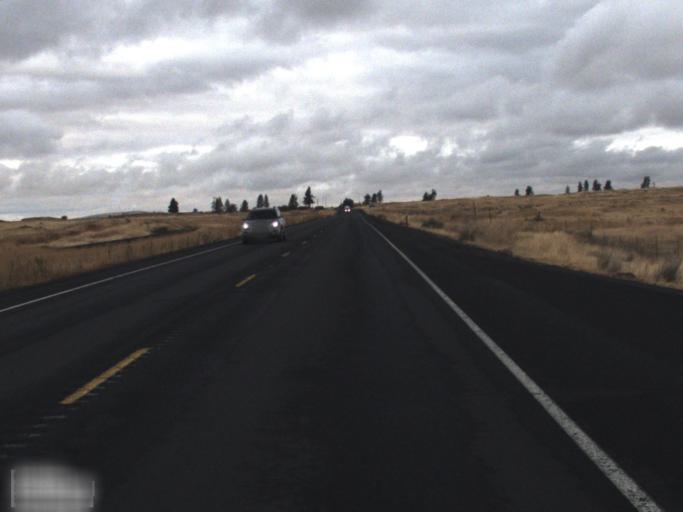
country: US
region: Washington
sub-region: Lincoln County
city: Davenport
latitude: 47.6899
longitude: -118.3880
